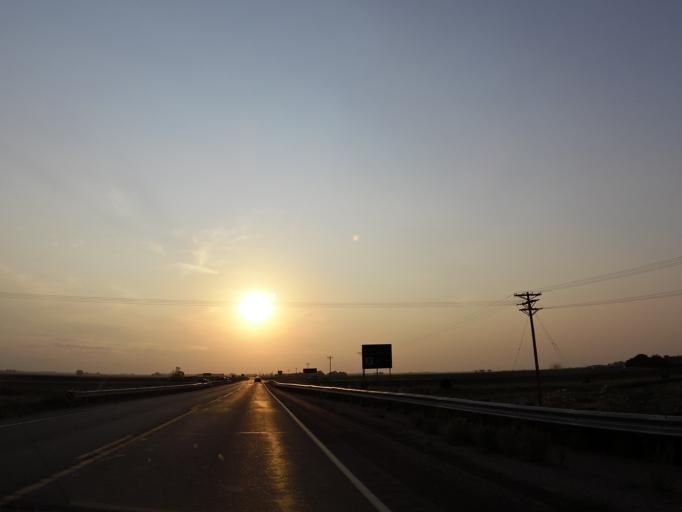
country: US
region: North Dakota
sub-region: Grand Forks County
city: Larimore
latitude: 47.7443
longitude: -97.6227
